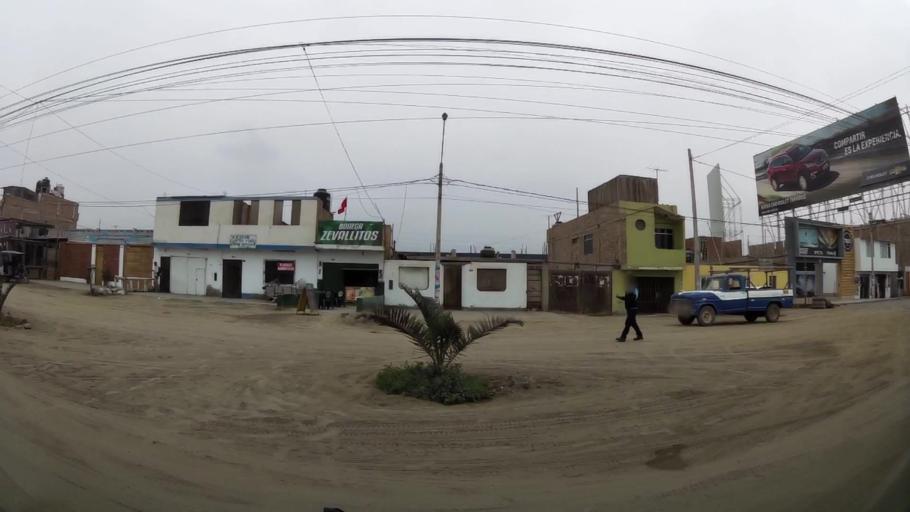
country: PE
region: Lima
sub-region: Lima
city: Punta Hermosa
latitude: -12.3176
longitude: -76.8316
